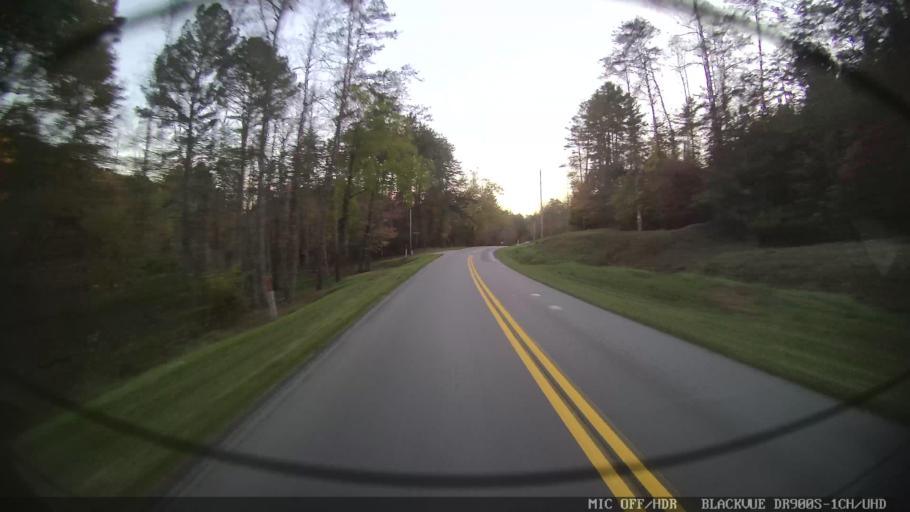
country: US
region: Georgia
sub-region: Union County
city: Blairsville
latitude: 34.8733
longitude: -83.8797
